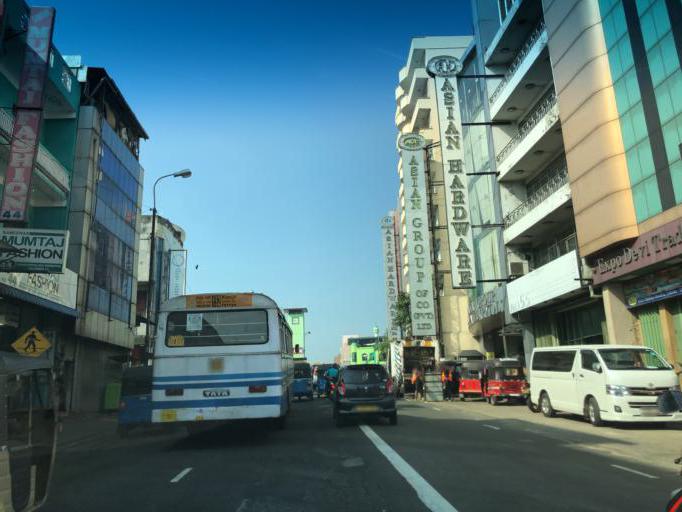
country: LK
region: Western
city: Colombo
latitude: 6.9420
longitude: 79.8609
